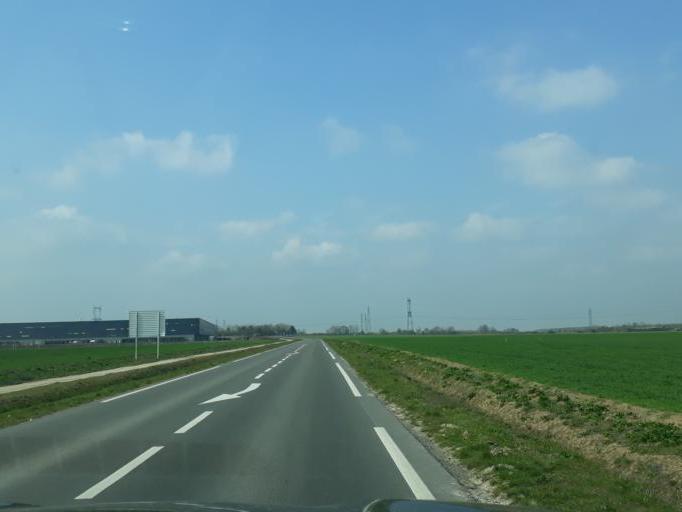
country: FR
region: Centre
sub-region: Departement du Loiret
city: Artenay
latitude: 48.0957
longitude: 1.8637
